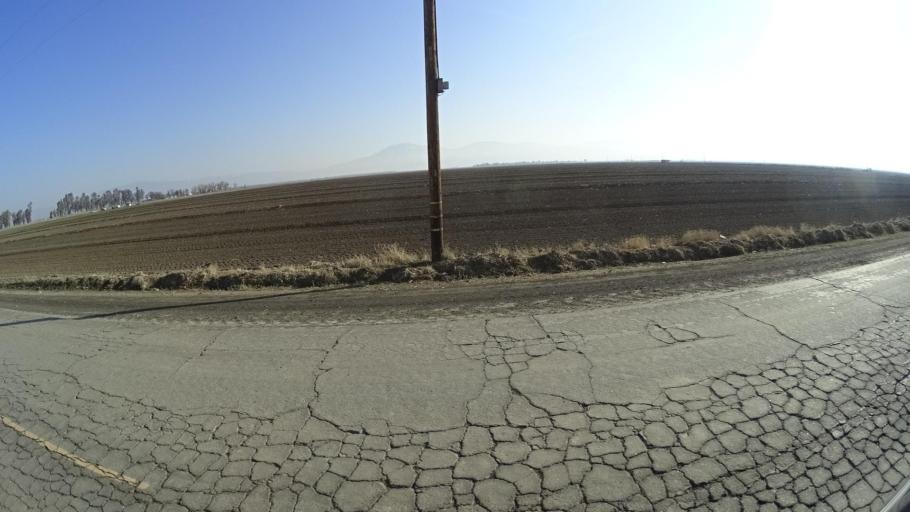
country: US
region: California
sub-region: Kern County
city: Weedpatch
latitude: 35.1813
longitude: -118.9679
